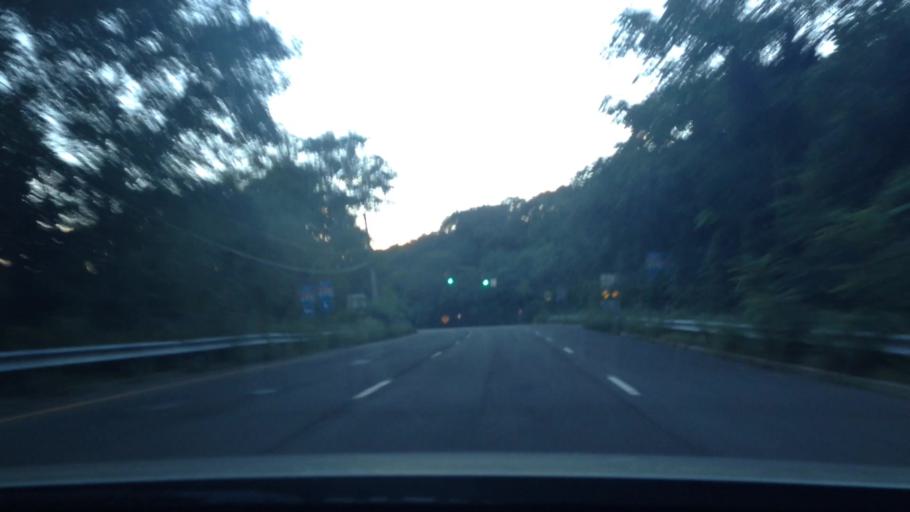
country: US
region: New York
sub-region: Suffolk County
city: Dix Hills
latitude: 40.7944
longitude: -73.3522
